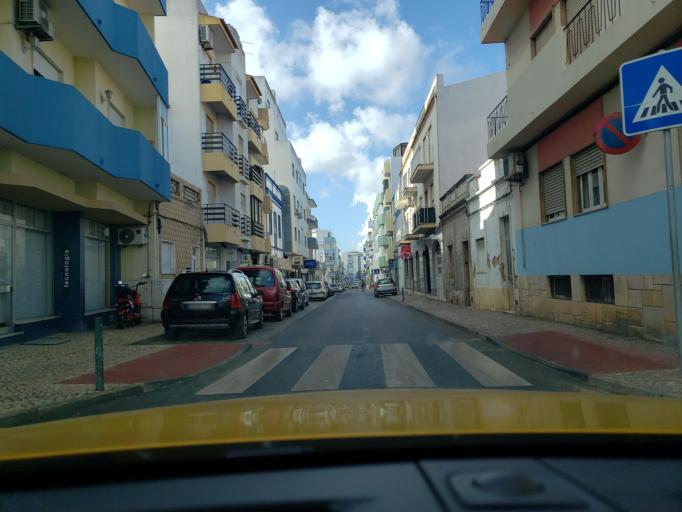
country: PT
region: Faro
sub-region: Portimao
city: Portimao
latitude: 37.1415
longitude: -8.5352
